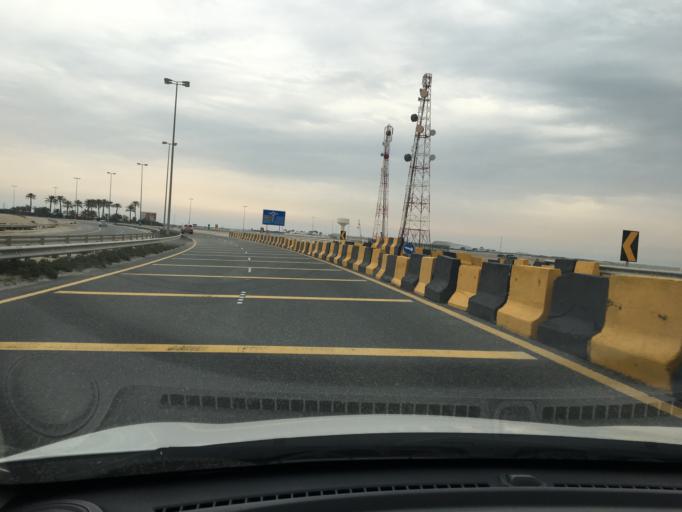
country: BH
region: Central Governorate
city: Dar Kulayb
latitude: 25.8483
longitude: 50.5836
